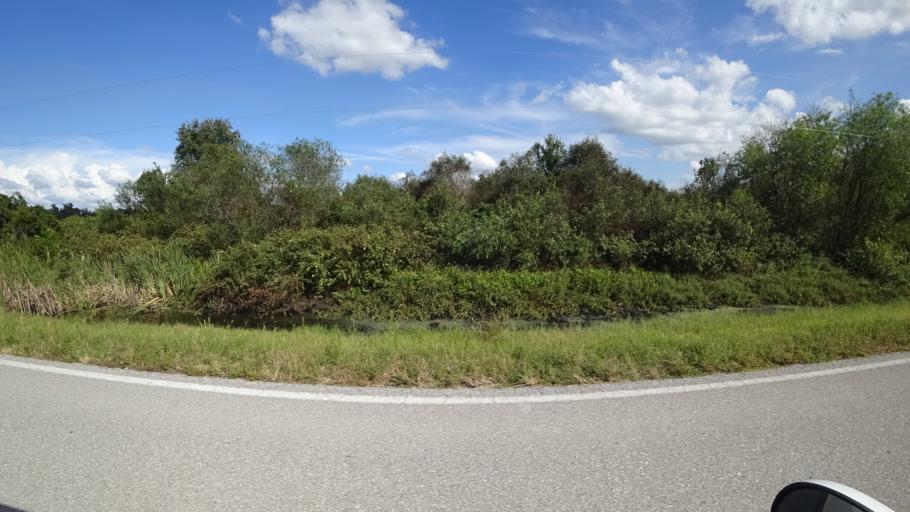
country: US
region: Florida
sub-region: DeSoto County
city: Arcadia
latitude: 27.2889
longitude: -82.0563
